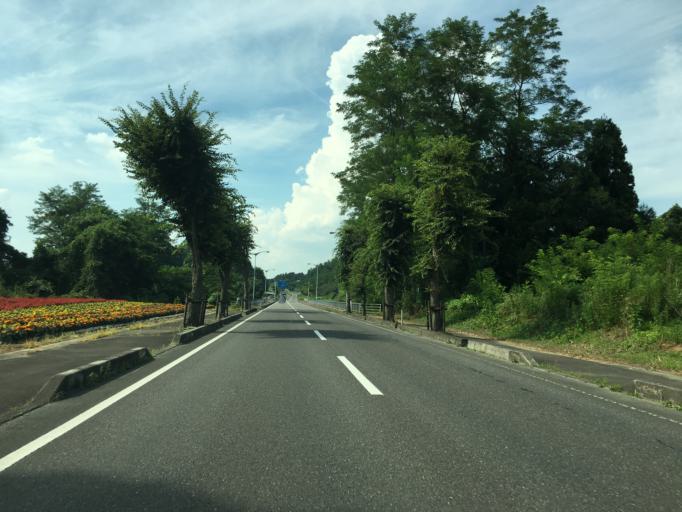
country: JP
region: Fukushima
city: Sukagawa
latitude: 37.2498
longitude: 140.4305
